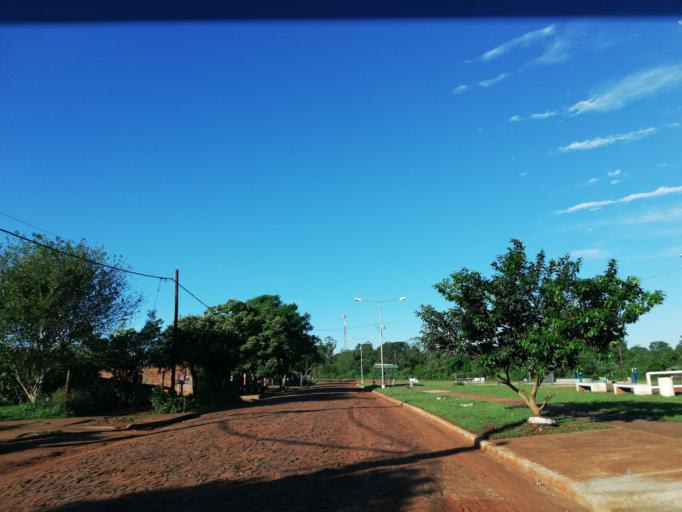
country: AR
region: Misiones
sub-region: Departamento de Capital
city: Posadas
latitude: -27.4367
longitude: -55.9364
